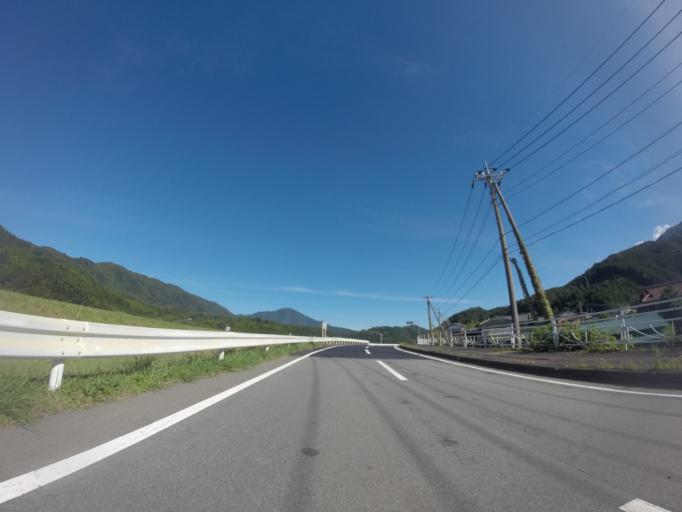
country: JP
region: Shizuoka
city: Fujinomiya
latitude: 35.3339
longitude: 138.4487
